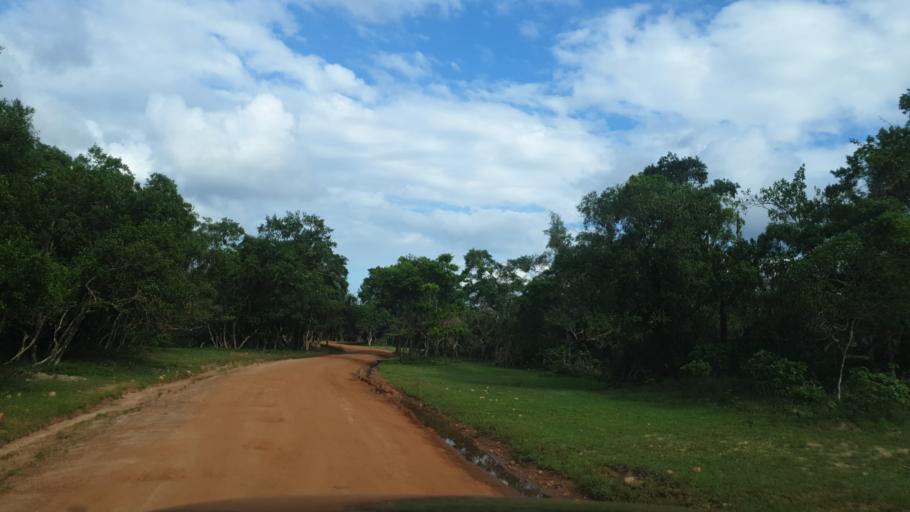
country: LK
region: North Central
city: Anuradhapura
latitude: 8.3638
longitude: 80.1019
